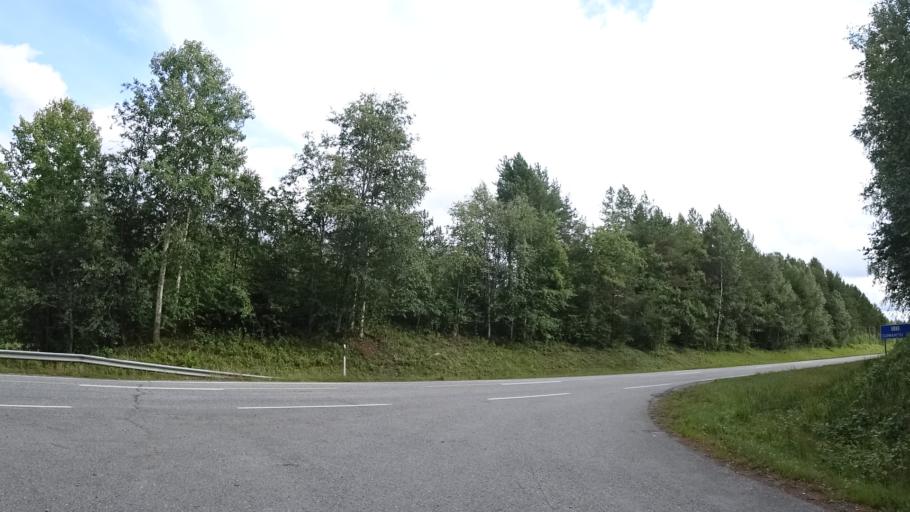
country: FI
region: North Karelia
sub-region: Joensuu
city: Ilomantsi
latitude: 62.7432
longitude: 30.9959
